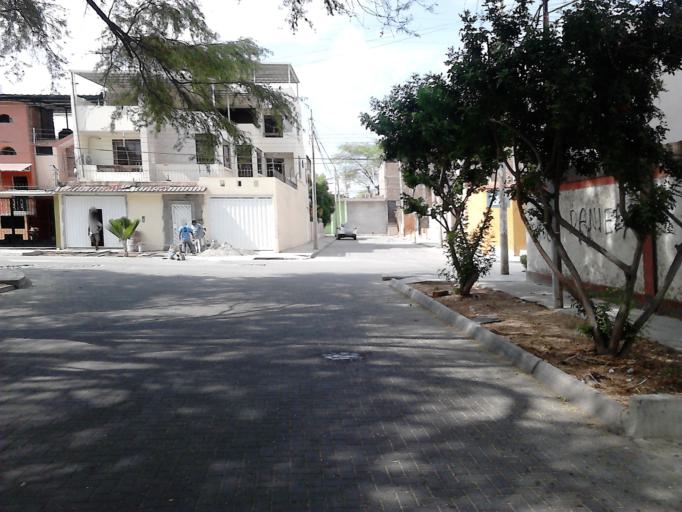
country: PE
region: Piura
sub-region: Provincia de Piura
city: Piura
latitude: -5.1899
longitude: -80.6448
